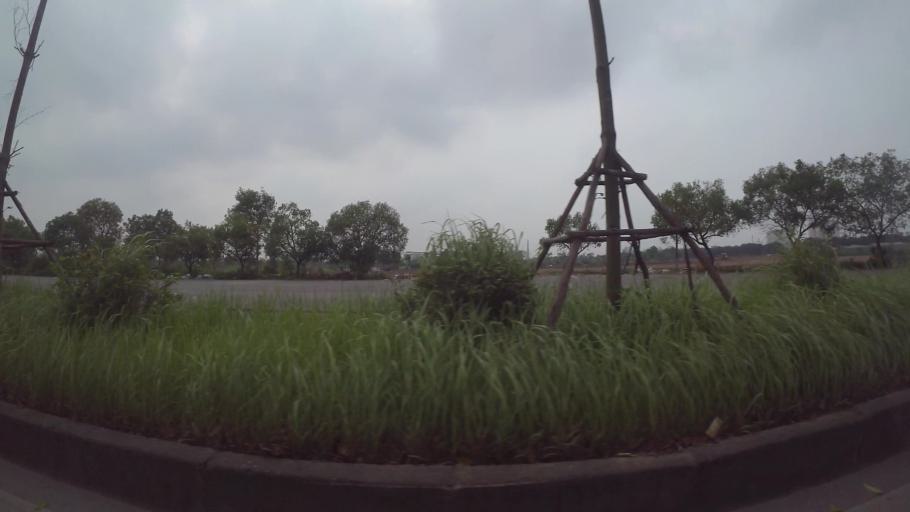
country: VN
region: Ha Noi
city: Trau Quy
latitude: 21.0609
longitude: 105.9074
